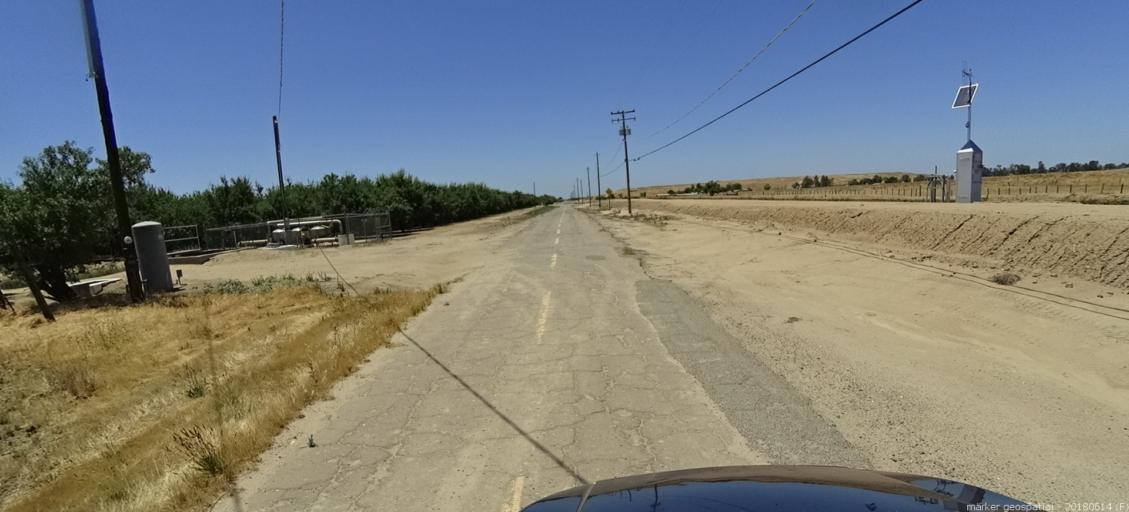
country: US
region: California
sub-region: Madera County
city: Fairmead
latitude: 37.0619
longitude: -120.1863
